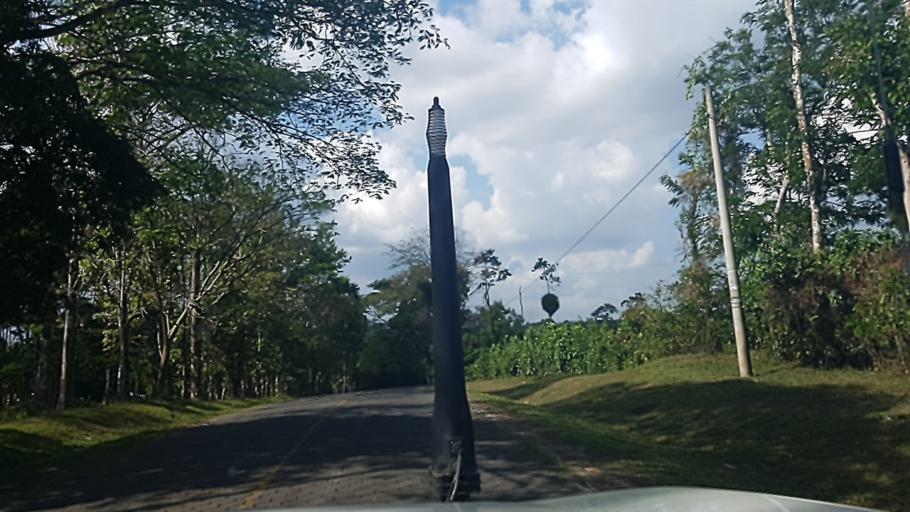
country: NI
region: Atlantico Sur
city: Nueva Guinea
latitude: 11.7016
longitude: -84.3843
